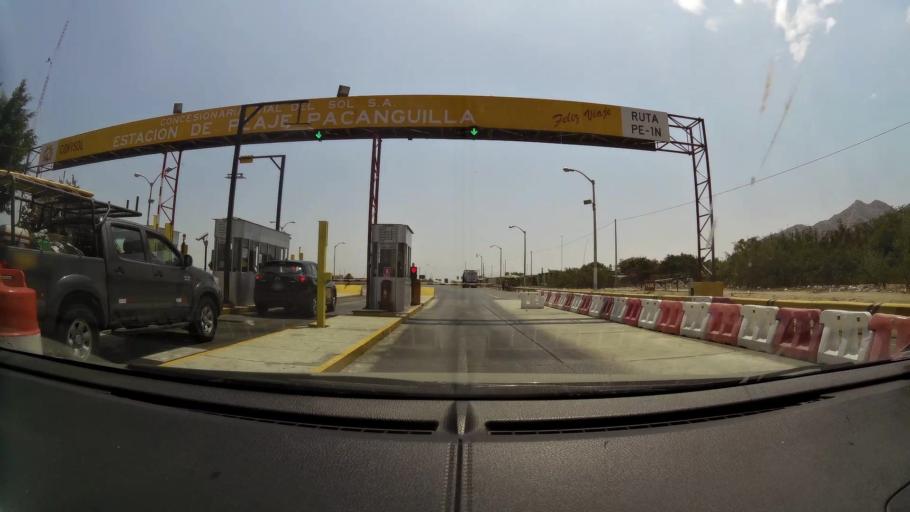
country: PE
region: La Libertad
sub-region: Chepen
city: Pacanga
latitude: -7.1118
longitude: -79.4968
